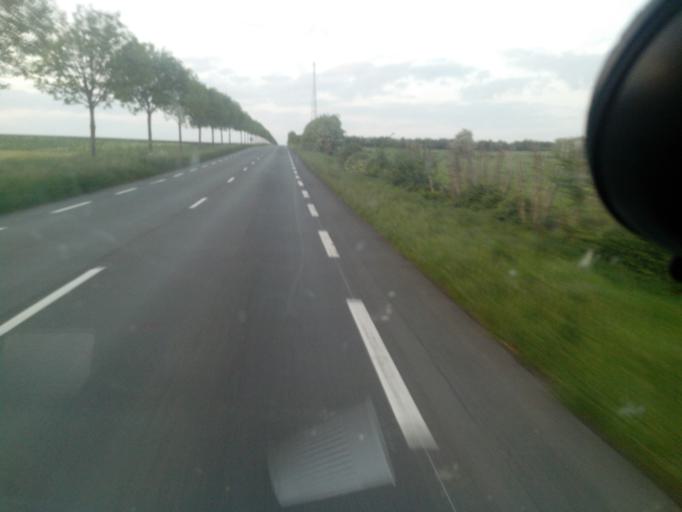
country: FR
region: Nord-Pas-de-Calais
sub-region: Departement du Pas-de-Calais
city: Marconnelle
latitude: 50.2898
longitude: 1.9945
